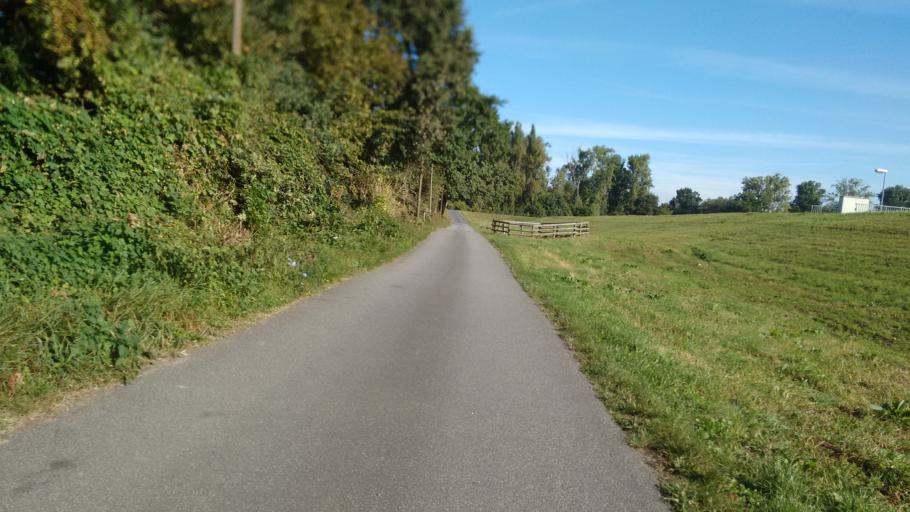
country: DE
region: Rheinland-Pfalz
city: Nieder-Ingelheim
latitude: 49.9985
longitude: 8.0647
